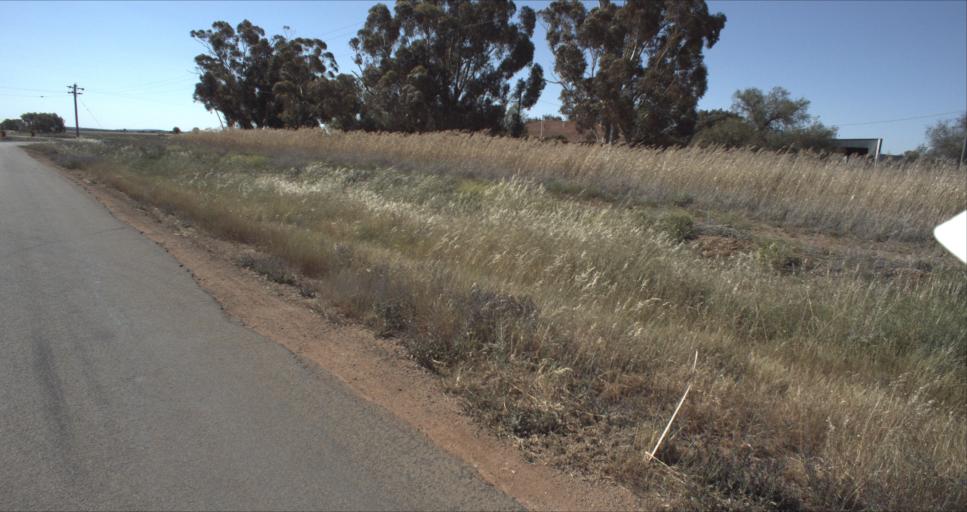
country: AU
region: New South Wales
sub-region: Leeton
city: Leeton
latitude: -34.4789
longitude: 146.3688
